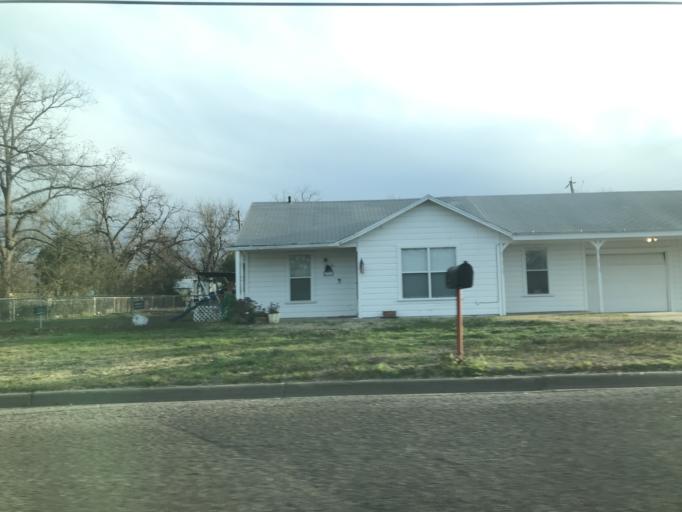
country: US
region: Texas
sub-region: Tom Green County
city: San Angelo
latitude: 31.4974
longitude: -100.4561
